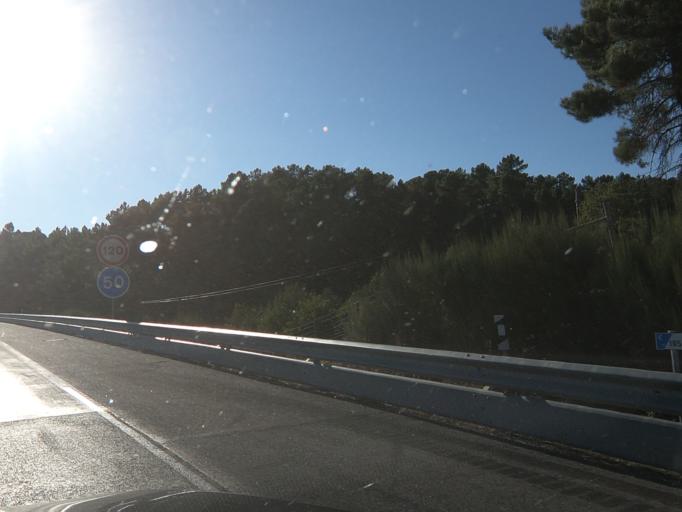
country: PT
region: Vila Real
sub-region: Sabrosa
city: Sabrosa
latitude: 41.3477
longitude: -7.6032
